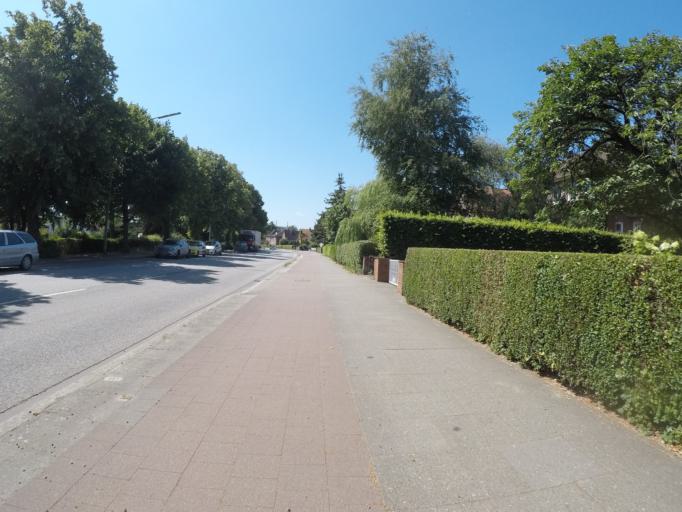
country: DE
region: Hamburg
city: Kleiner Grasbrook
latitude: 53.4941
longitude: 10.0202
